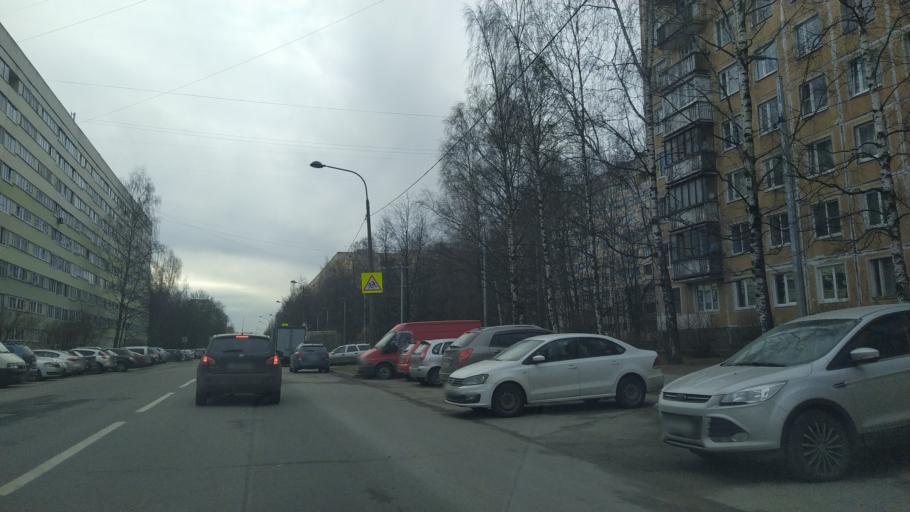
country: RU
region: St.-Petersburg
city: Grazhdanka
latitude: 60.0299
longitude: 30.4262
